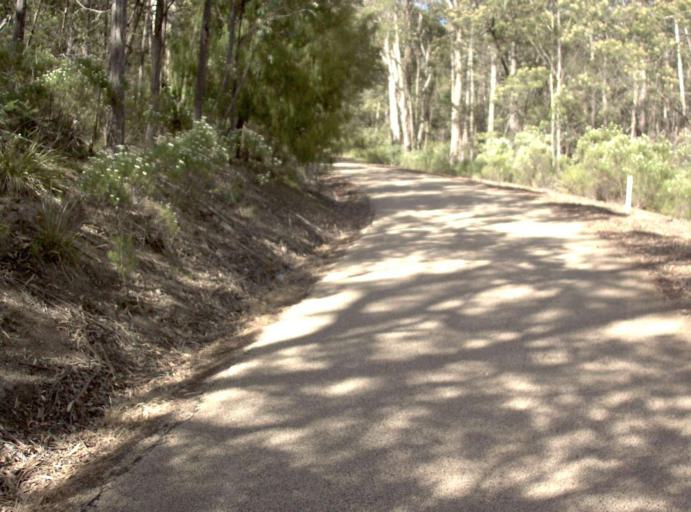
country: AU
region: Victoria
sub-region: East Gippsland
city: Lakes Entrance
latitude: -37.4107
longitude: 148.1225
